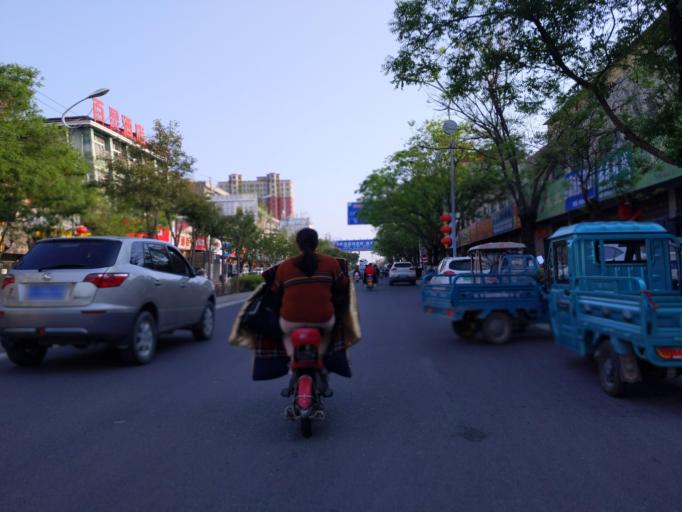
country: CN
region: Henan Sheng
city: Puyang Chengguanzhen
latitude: 35.7005
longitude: 115.0162
